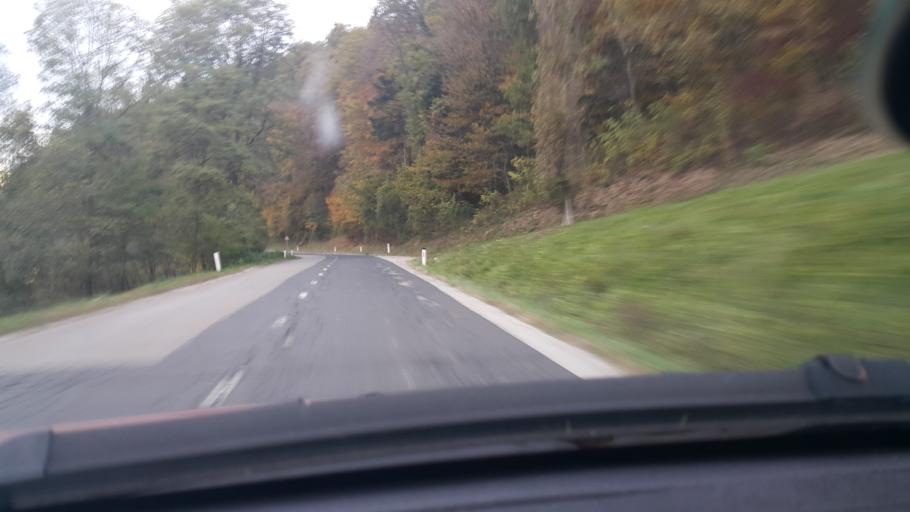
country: SI
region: Kungota
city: Zgornja Kungota
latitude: 46.6435
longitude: 15.5832
